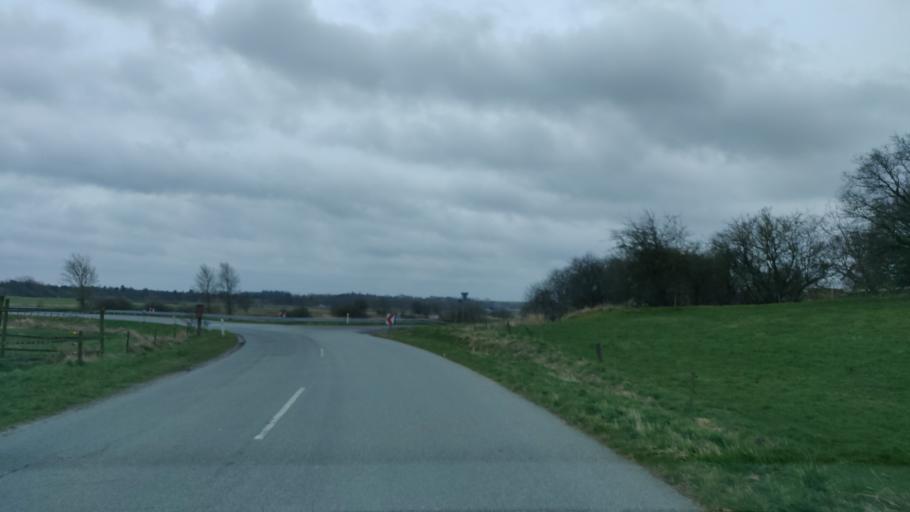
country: DK
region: Central Jutland
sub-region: Skive Kommune
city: Hojslev
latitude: 56.5712
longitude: 9.2374
